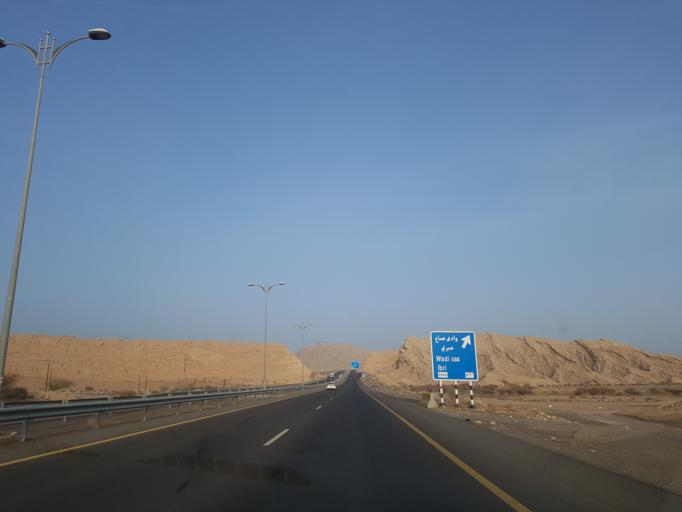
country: OM
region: Al Buraimi
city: Al Buraymi
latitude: 24.2335
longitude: 55.9422
